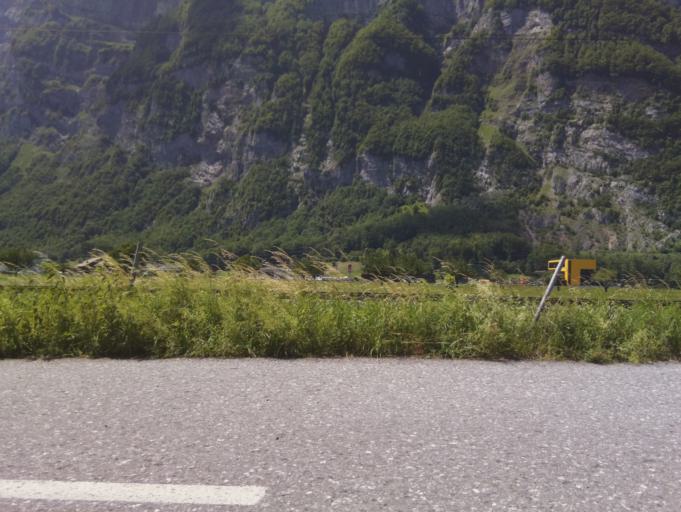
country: CH
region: Glarus
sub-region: Glarus
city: Netstal
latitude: 47.0726
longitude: 9.0594
